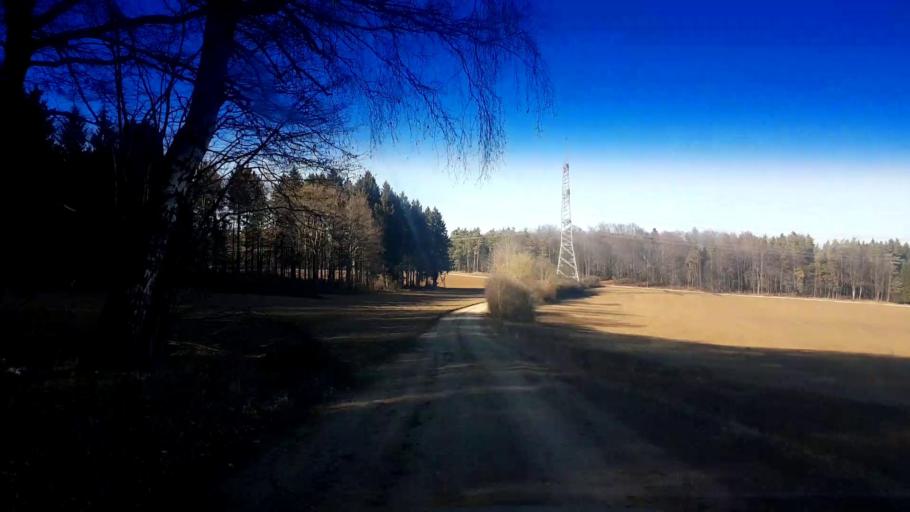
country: DE
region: Bavaria
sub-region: Upper Franconia
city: Poxdorf
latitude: 49.9639
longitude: 11.0860
